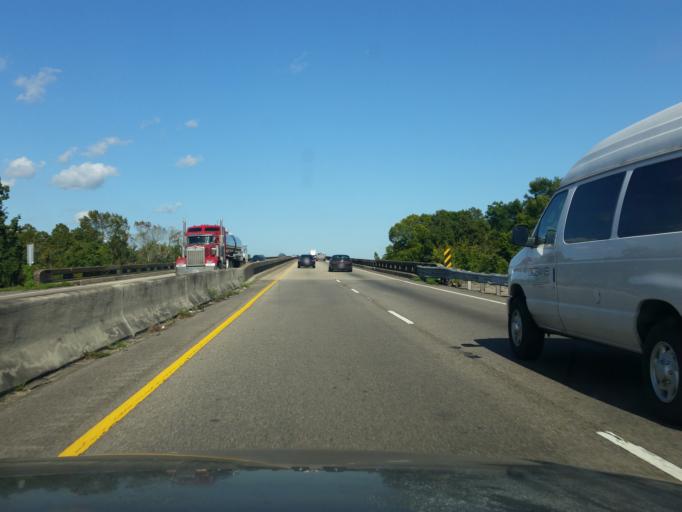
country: US
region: Mississippi
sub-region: Hancock County
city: Pearlington
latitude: 30.3015
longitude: -89.6500
